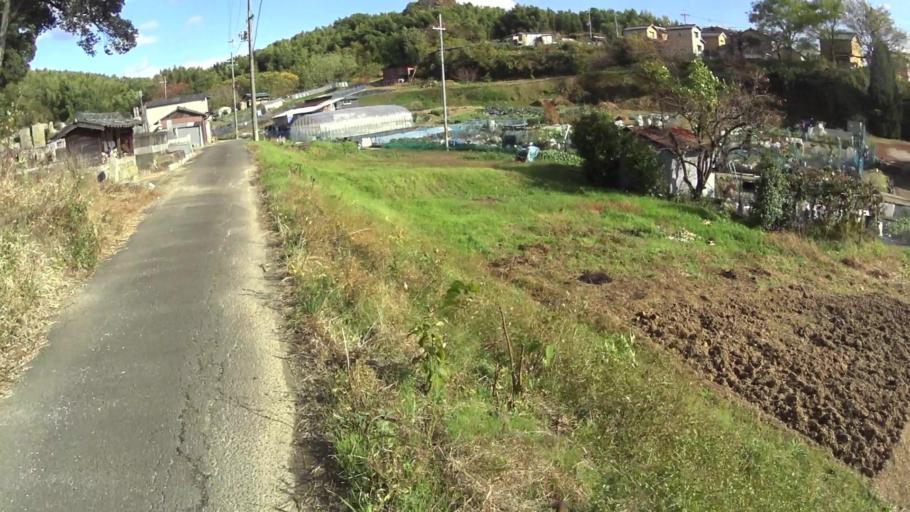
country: JP
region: Kyoto
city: Kyoto
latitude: 34.9600
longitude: 135.7787
